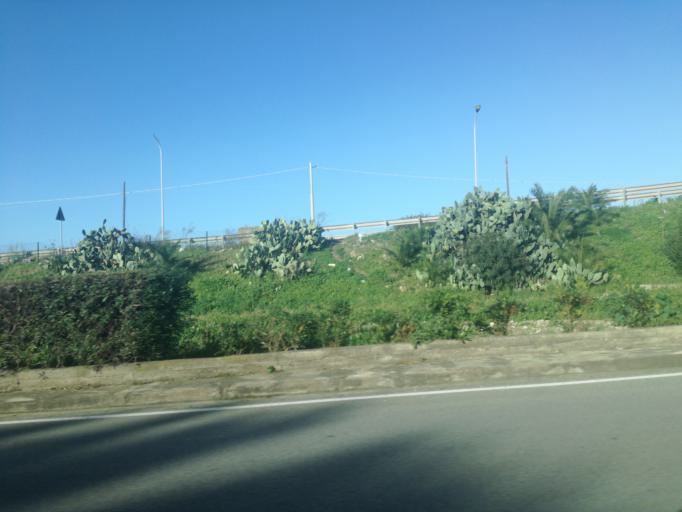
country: IT
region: Sicily
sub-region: Provincia di Caltanissetta
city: Gela
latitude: 37.0625
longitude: 14.2663
